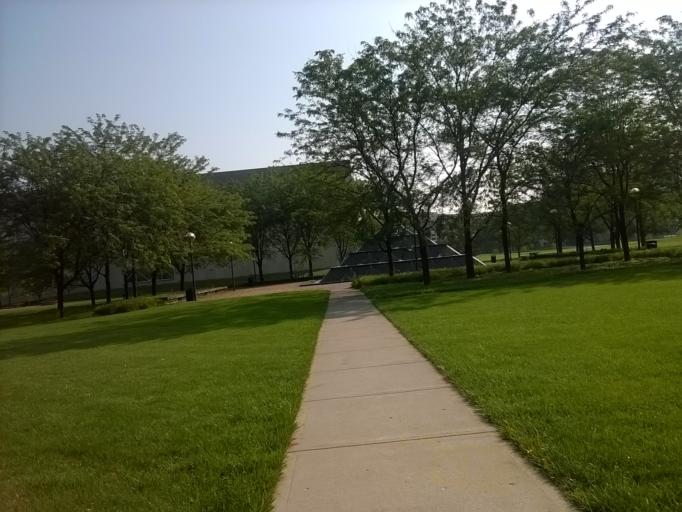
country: US
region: Indiana
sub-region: Marion County
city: Indianapolis
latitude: 39.7718
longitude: -86.1732
